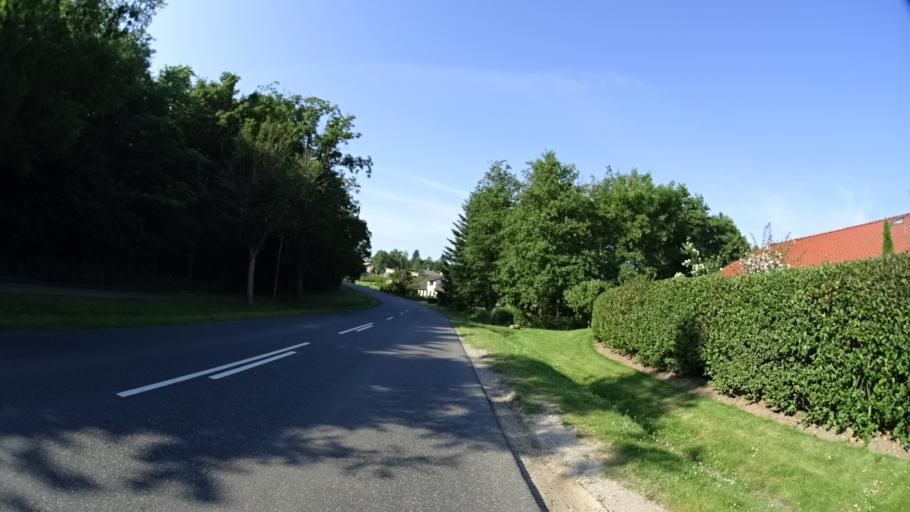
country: DK
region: Central Jutland
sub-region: Arhus Kommune
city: Stavtrup
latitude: 56.1357
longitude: 10.1168
